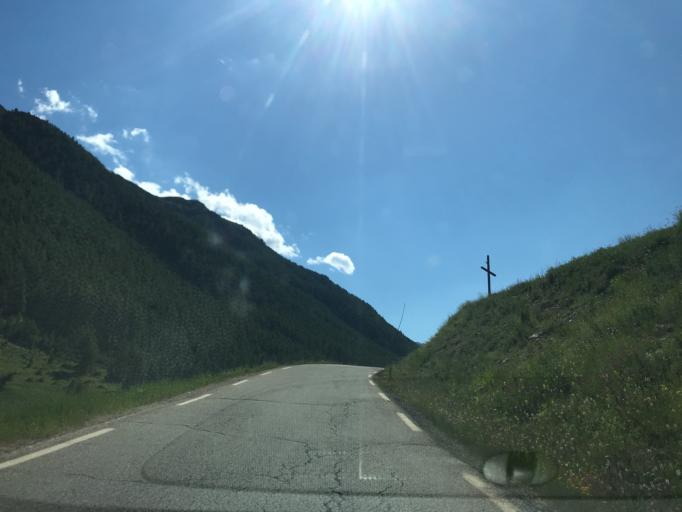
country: IT
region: Piedmont
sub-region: Provincia di Cuneo
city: Pontechianale
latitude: 44.7202
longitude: 6.8960
